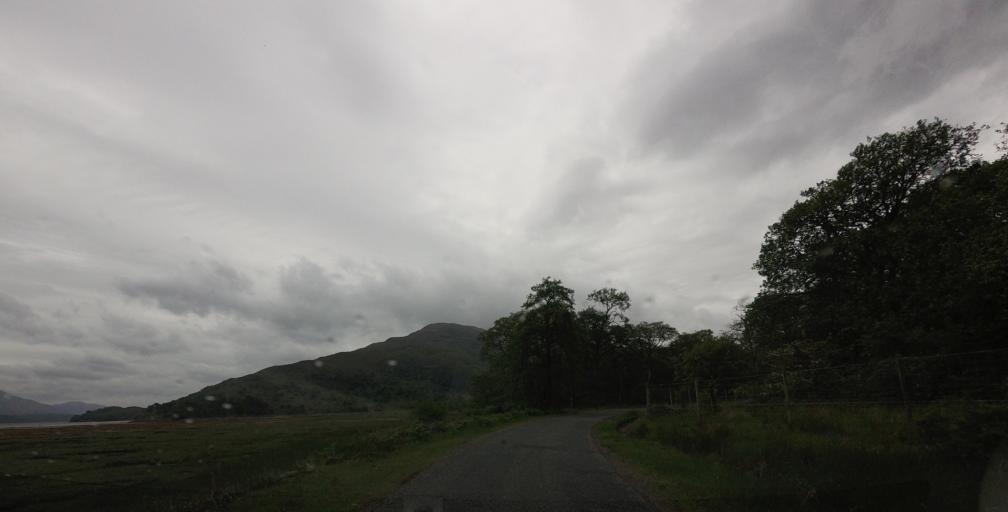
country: GB
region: Scotland
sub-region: Highland
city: Fort William
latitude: 56.7691
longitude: -5.2267
